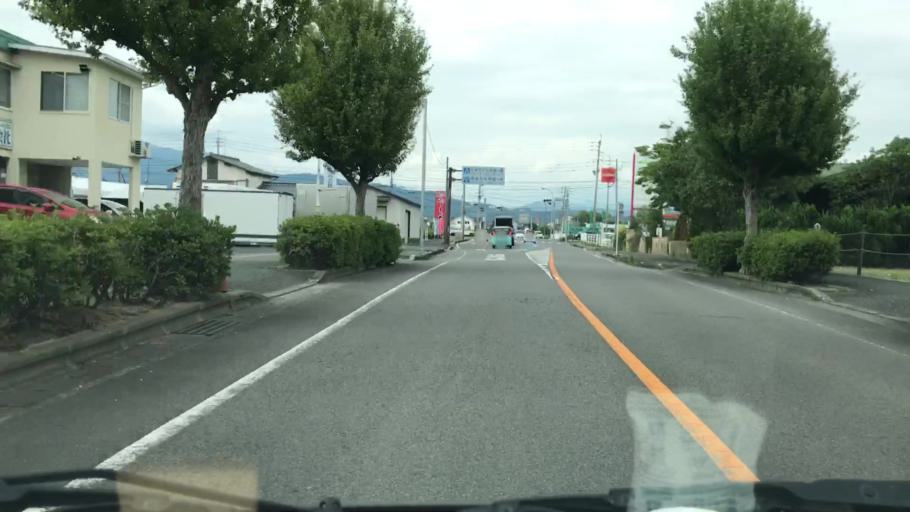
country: JP
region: Saga Prefecture
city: Saga-shi
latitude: 33.2677
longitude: 130.2619
